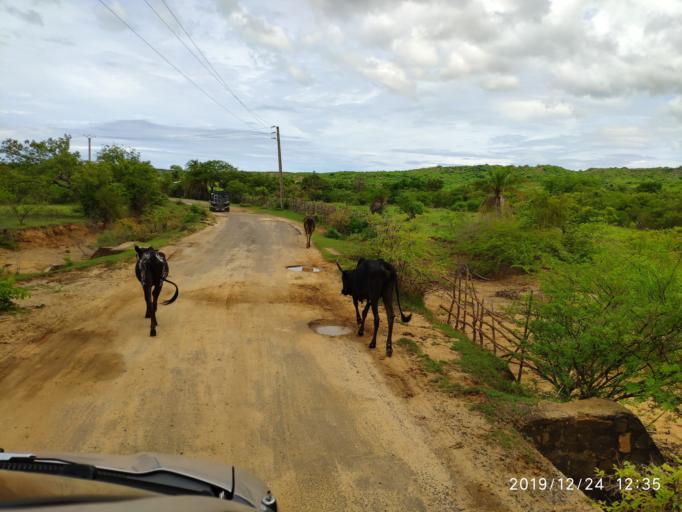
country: MG
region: Diana
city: Antsiranana
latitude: -12.3119
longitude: 49.3449
